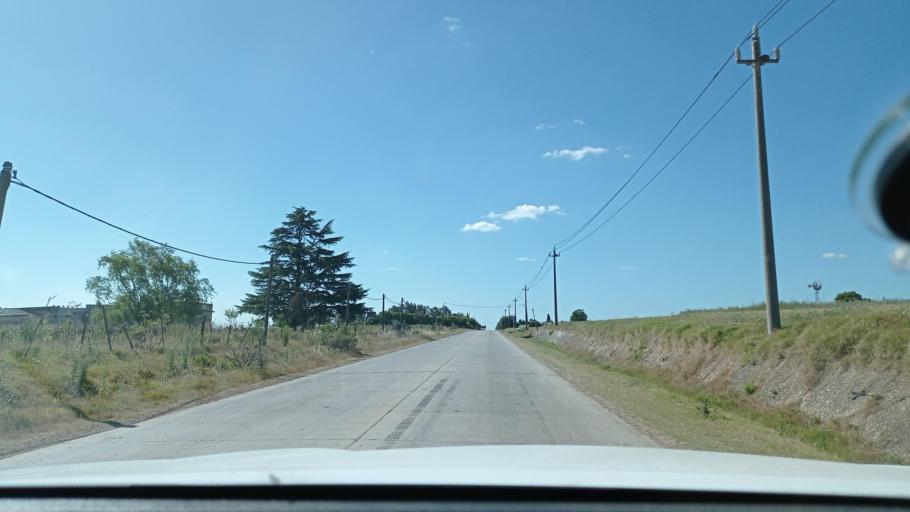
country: UY
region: Canelones
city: La Paz
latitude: -34.7771
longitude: -56.2577
